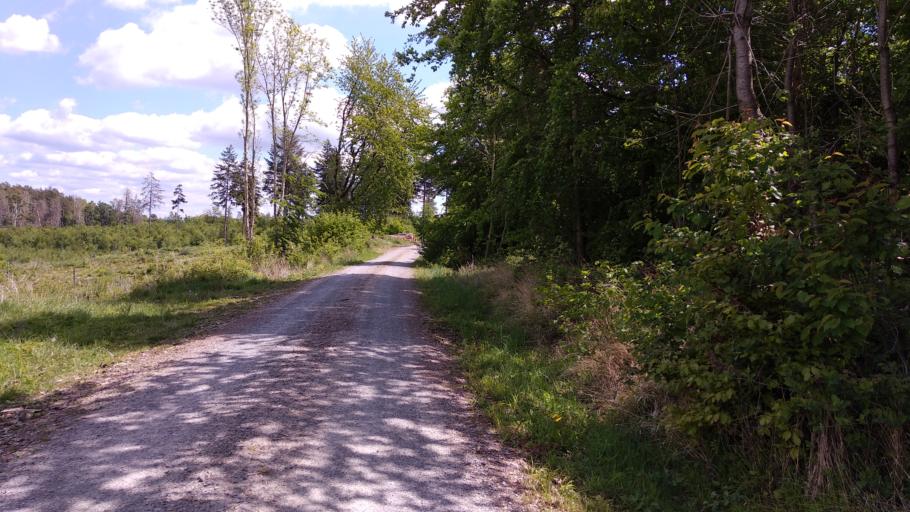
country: DE
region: North Rhine-Westphalia
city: Beverungen
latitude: 51.6717
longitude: 9.3309
